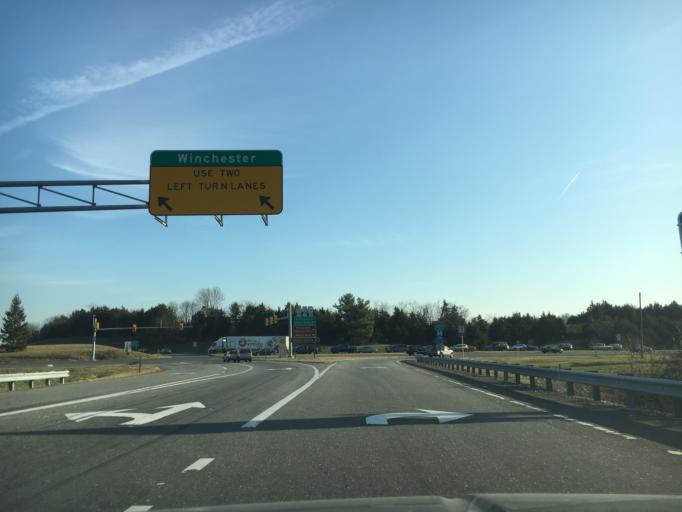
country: US
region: Virginia
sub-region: Warren County
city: Front Royal
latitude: 38.9608
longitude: -78.1942
